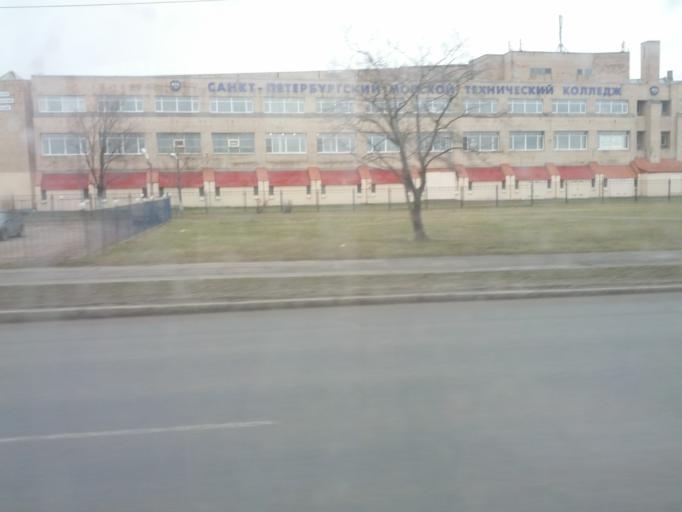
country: RU
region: St.-Petersburg
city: Obukhovo
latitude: 59.9030
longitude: 30.4574
